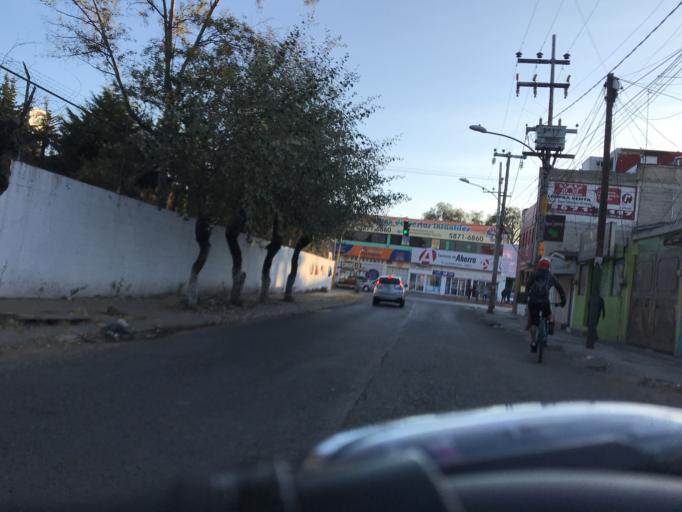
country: MX
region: Mexico
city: Cuautitlan Izcalli
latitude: 19.6599
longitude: -99.2110
